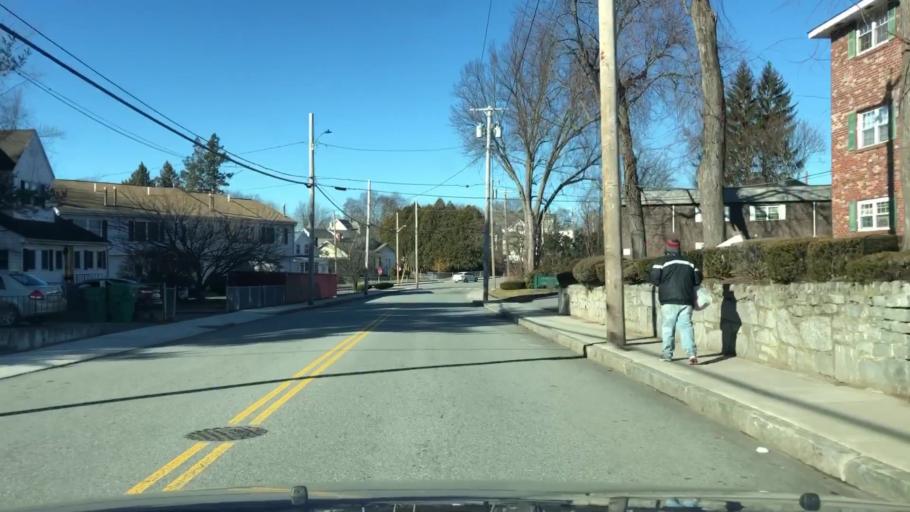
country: US
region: Massachusetts
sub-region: Middlesex County
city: Dracut
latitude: 42.6625
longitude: -71.3102
